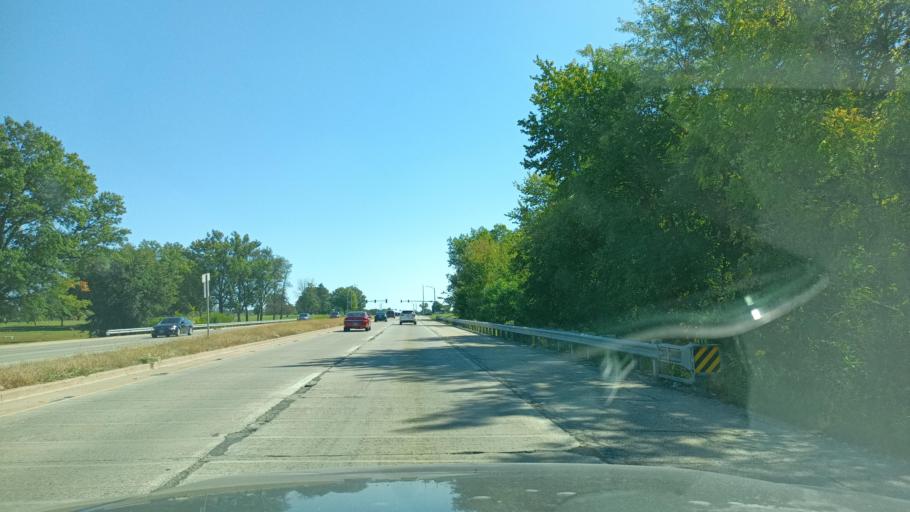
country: US
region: Illinois
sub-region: Peoria County
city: West Peoria
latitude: 40.7733
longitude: -89.6641
